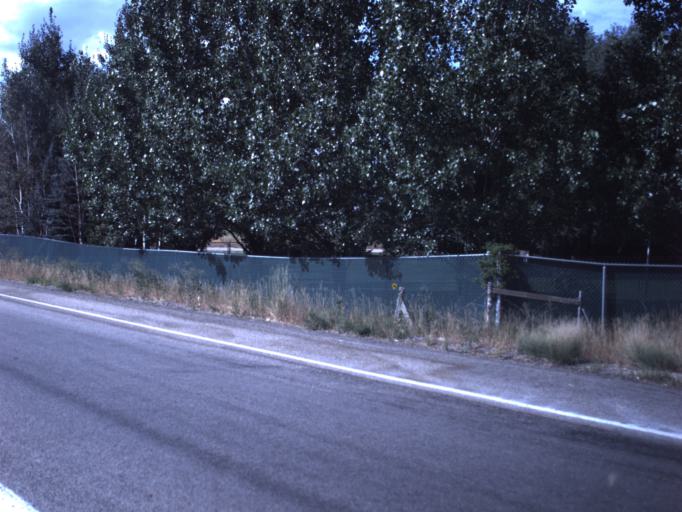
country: US
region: Utah
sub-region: Wasatch County
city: Heber
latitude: 40.4627
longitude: -111.3824
